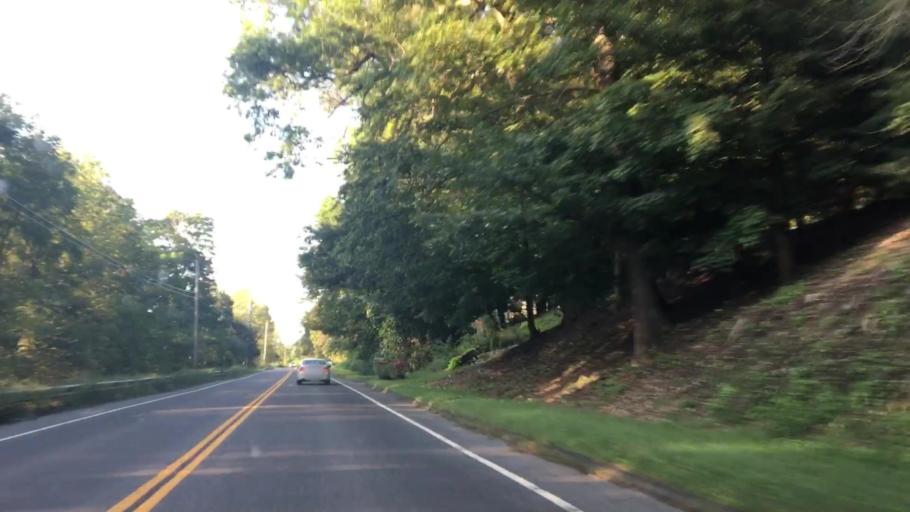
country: US
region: Connecticut
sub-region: Litchfield County
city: New Milford
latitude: 41.5539
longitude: -73.4055
